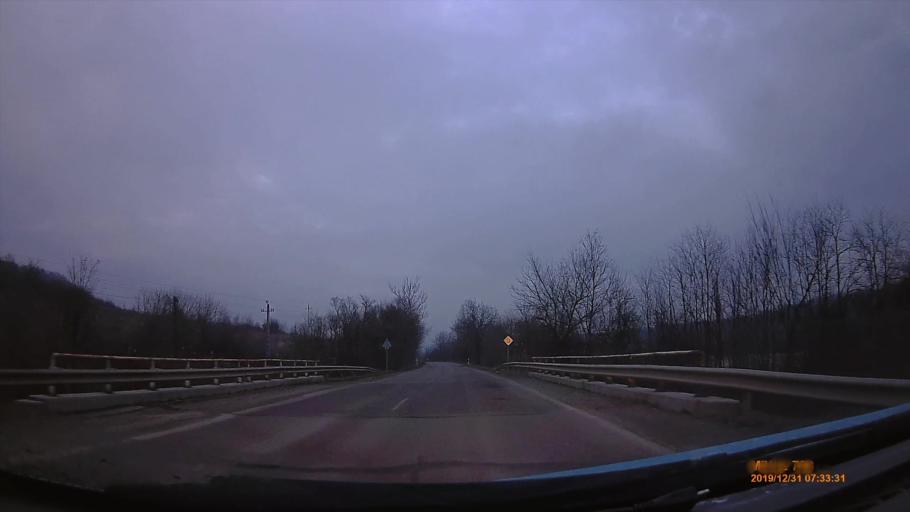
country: HU
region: Heves
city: Recsk
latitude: 47.9254
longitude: 20.1357
